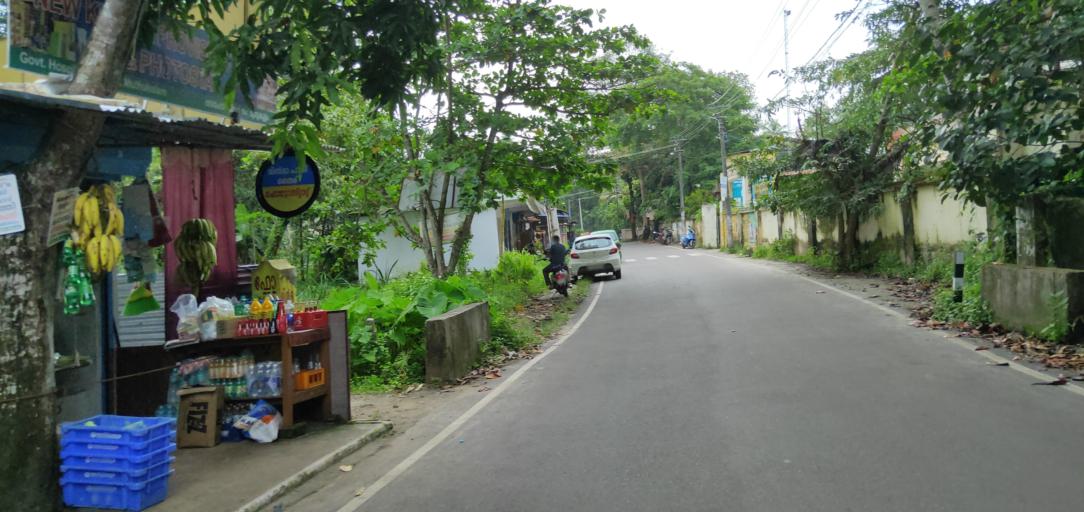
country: IN
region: Kerala
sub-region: Alappuzha
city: Kayankulam
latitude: 9.2169
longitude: 76.4563
